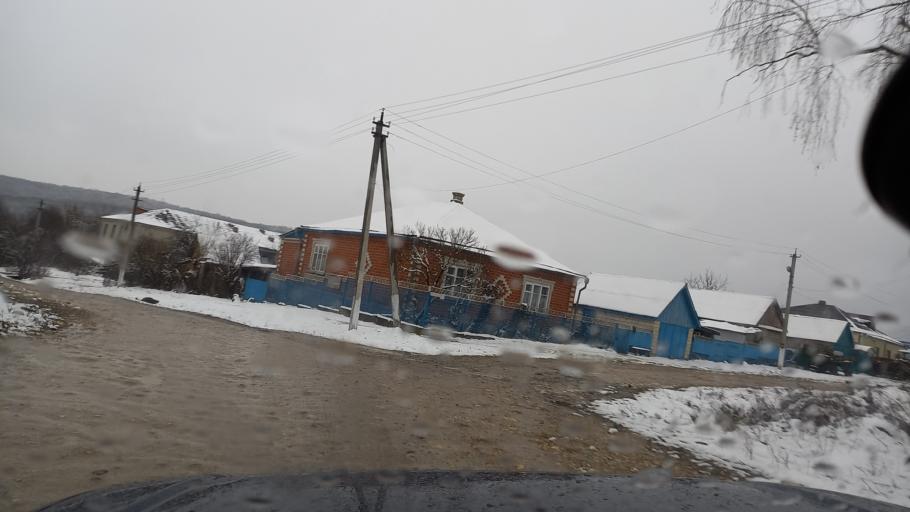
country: RU
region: Adygeya
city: Abadzekhskaya
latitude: 44.3516
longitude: 40.4112
